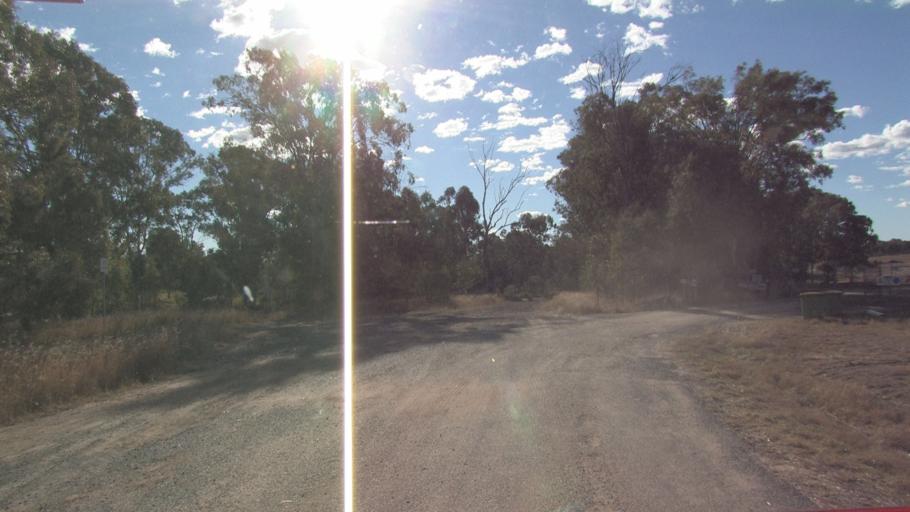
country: AU
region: Queensland
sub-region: Logan
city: North Maclean
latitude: -27.8211
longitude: 153.0059
